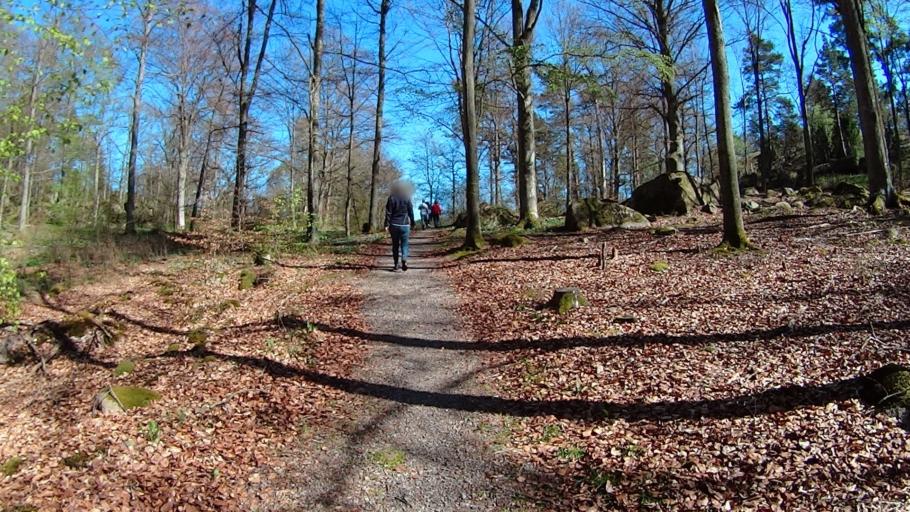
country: SE
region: Blekinge
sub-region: Ronneby Kommun
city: Brakne-Hoby
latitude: 56.1742
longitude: 15.0861
